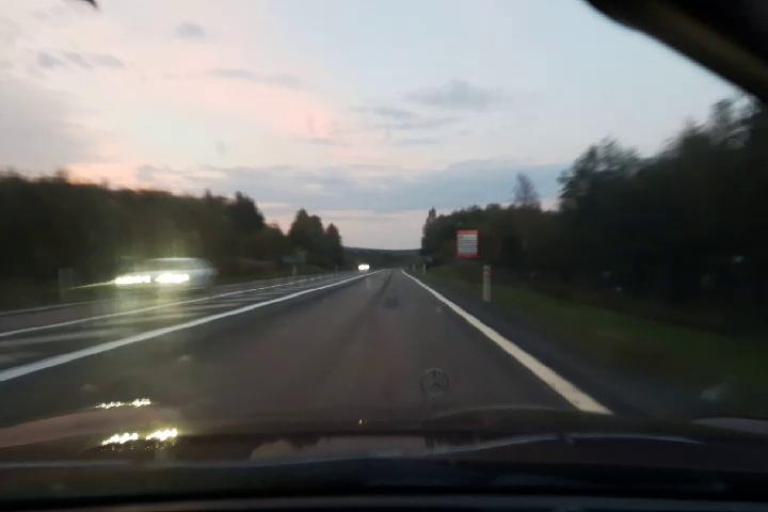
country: SE
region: Vaesternorrland
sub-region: Haernoesands Kommun
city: Haernoesand
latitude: 62.8698
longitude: 18.0412
